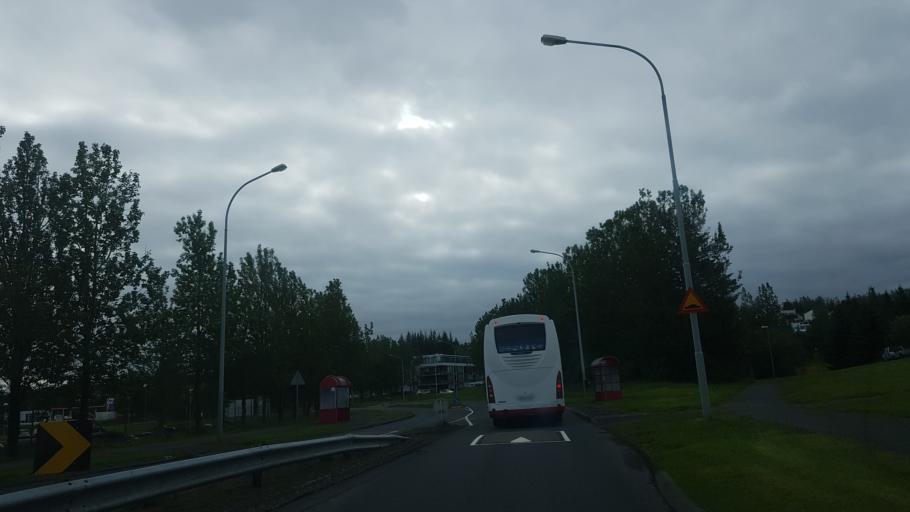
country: IS
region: Capital Region
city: Reykjavik
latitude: 64.1027
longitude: -21.8514
